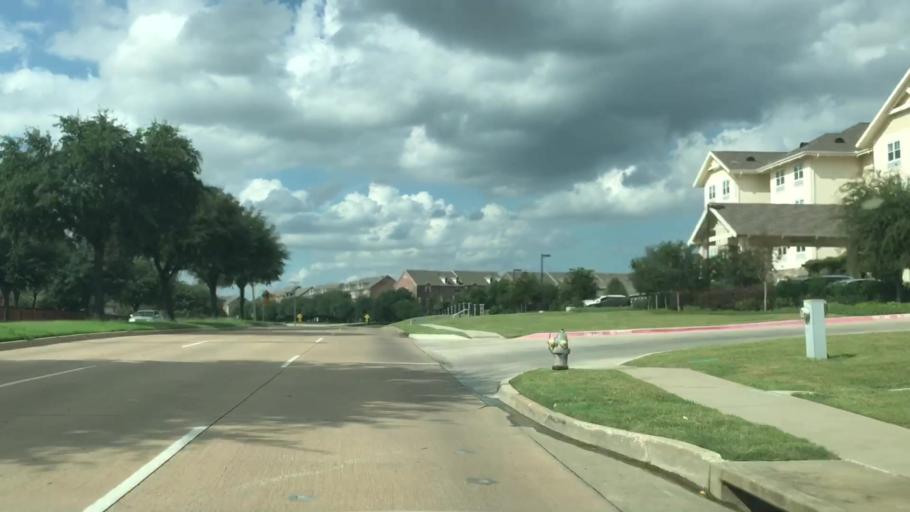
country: US
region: Texas
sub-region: Dallas County
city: Coppell
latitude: 32.9111
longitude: -96.9640
